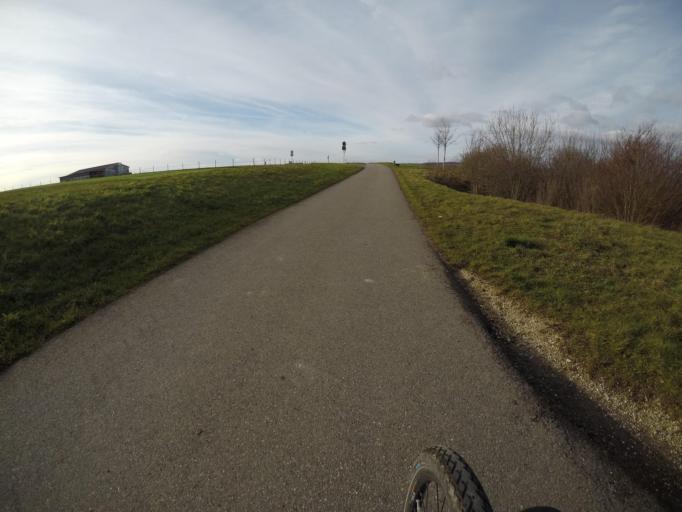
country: DE
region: Baden-Wuerttemberg
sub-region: Regierungsbezirk Stuttgart
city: Oberboihingen
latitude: 48.6300
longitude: 9.3703
